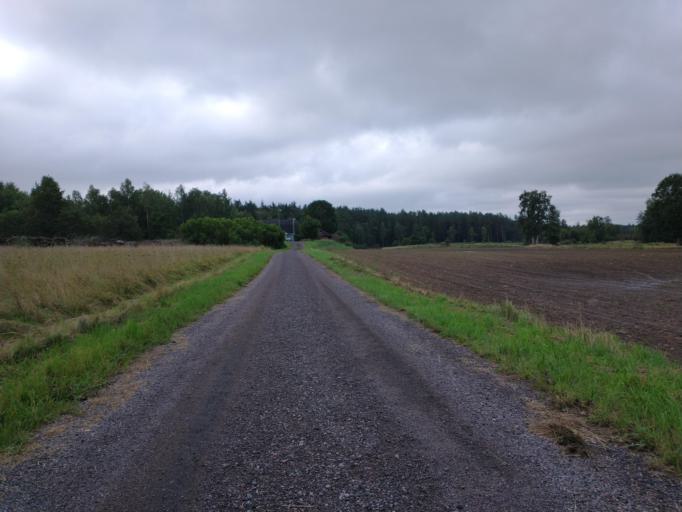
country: SE
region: Kalmar
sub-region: Kalmar Kommun
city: Lindsdal
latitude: 56.7804
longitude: 16.2967
